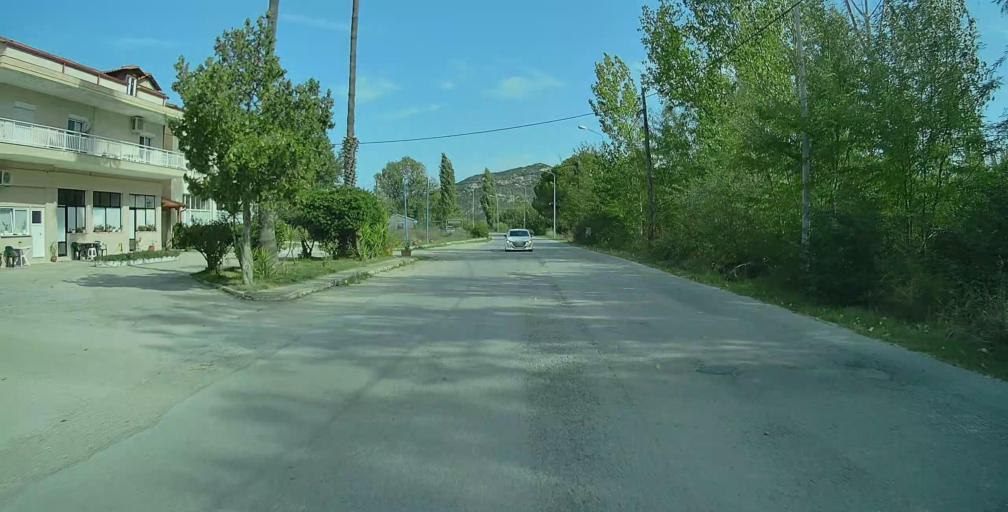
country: GR
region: Central Macedonia
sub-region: Nomos Chalkidikis
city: Sykia
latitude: 40.0343
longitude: 23.9610
